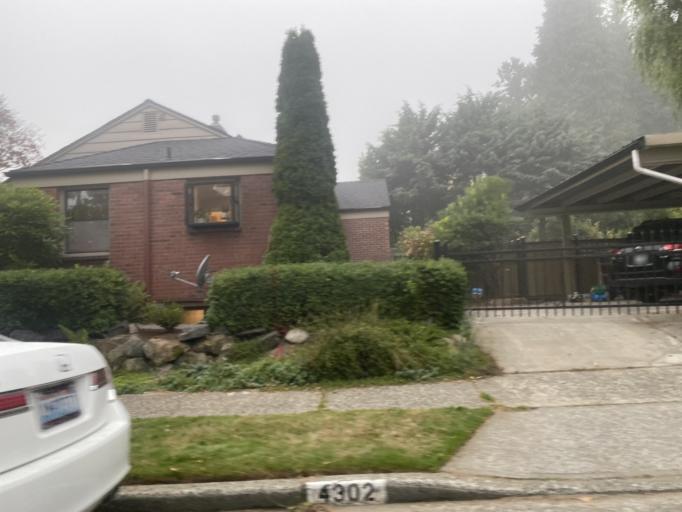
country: US
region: Washington
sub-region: King County
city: Seattle
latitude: 47.6507
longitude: -122.4122
